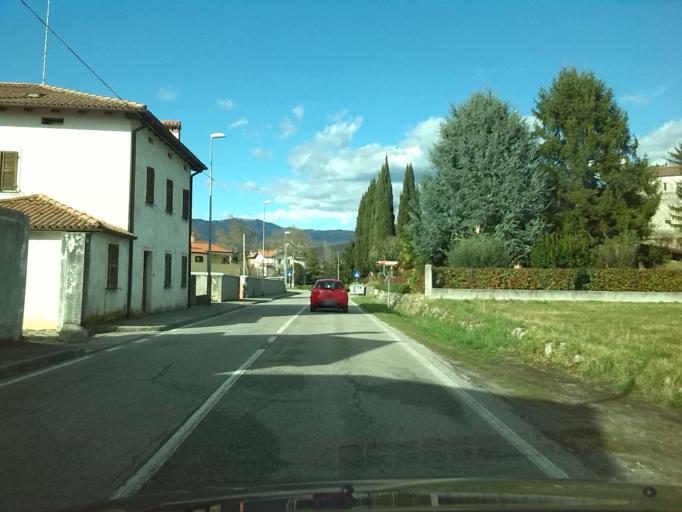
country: IT
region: Friuli Venezia Giulia
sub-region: Provincia di Udine
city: Cividale del Friuli
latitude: 46.0856
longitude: 13.4358
